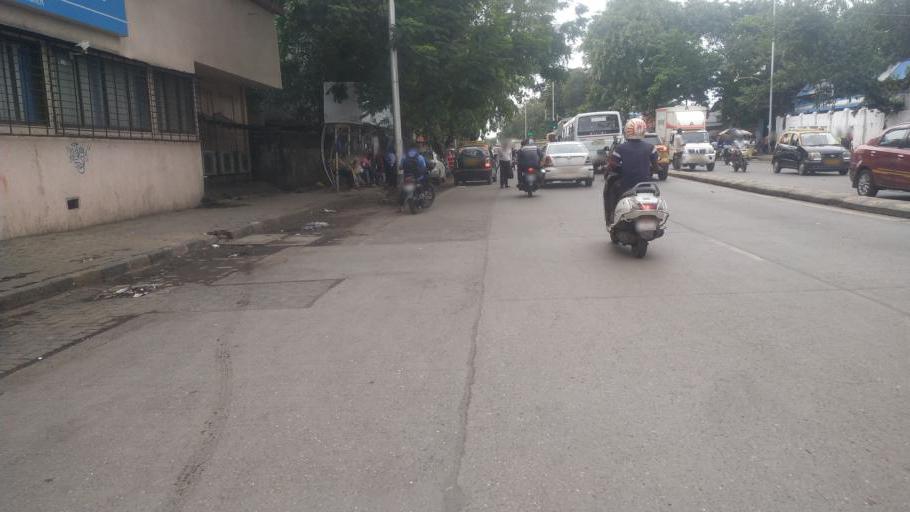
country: IN
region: Maharashtra
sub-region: Mumbai Suburban
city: Mumbai
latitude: 19.0389
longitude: 72.8470
